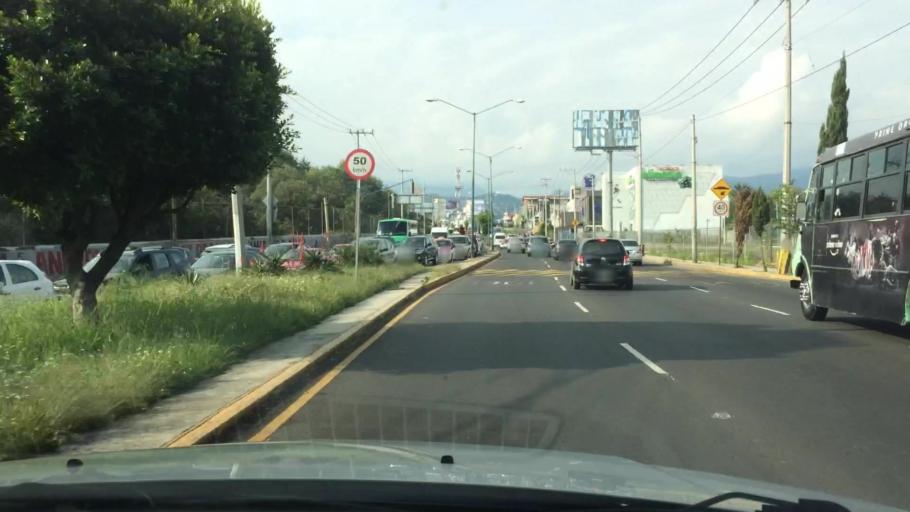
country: MX
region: Mexico City
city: Magdalena Contreras
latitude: 19.2956
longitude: -99.2146
